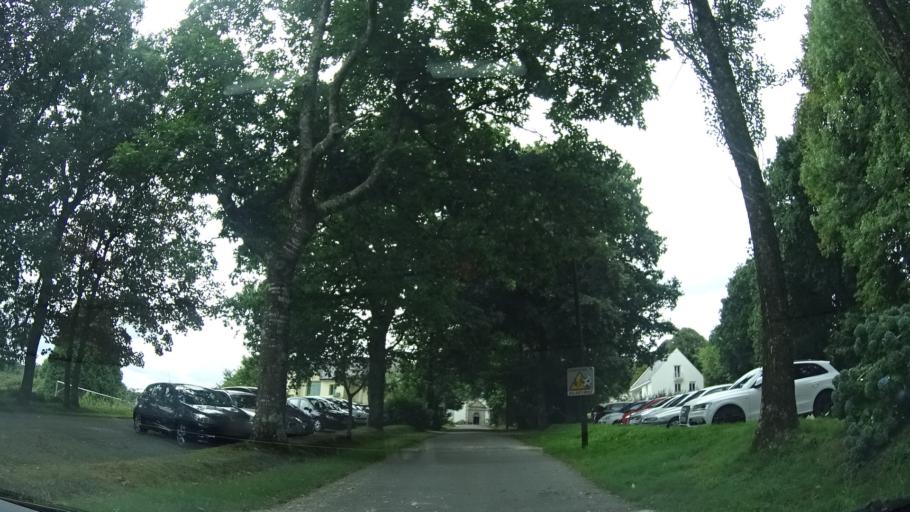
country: FR
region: Brittany
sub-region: Departement du Finistere
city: Chateaulin
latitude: 48.1976
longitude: -4.1067
